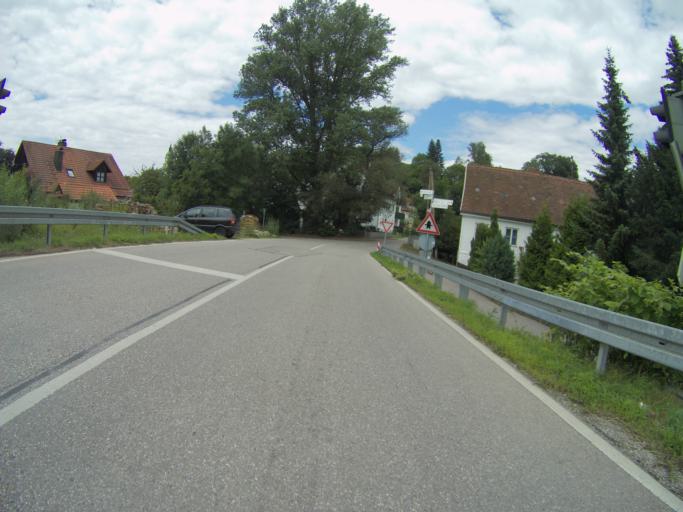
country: DE
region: Bavaria
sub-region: Upper Bavaria
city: Freising
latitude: 48.4058
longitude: 11.7627
